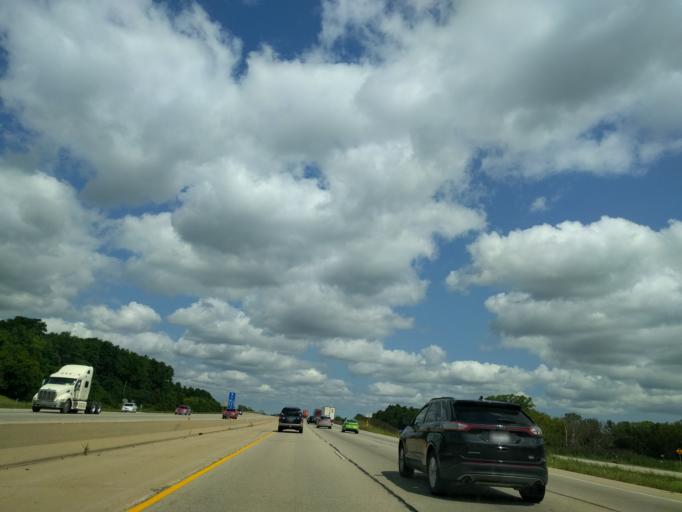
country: US
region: Wisconsin
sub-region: Kenosha County
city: Somers
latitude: 42.6662
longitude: -87.9529
